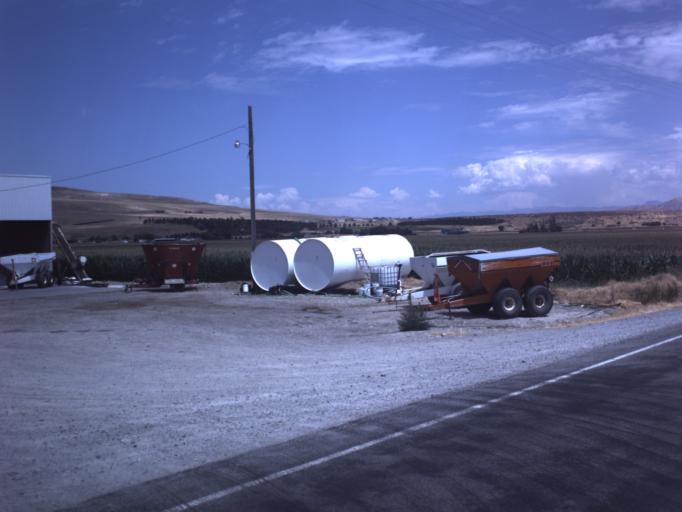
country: US
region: Utah
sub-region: Box Elder County
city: Tremonton
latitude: 41.7098
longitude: -112.2499
